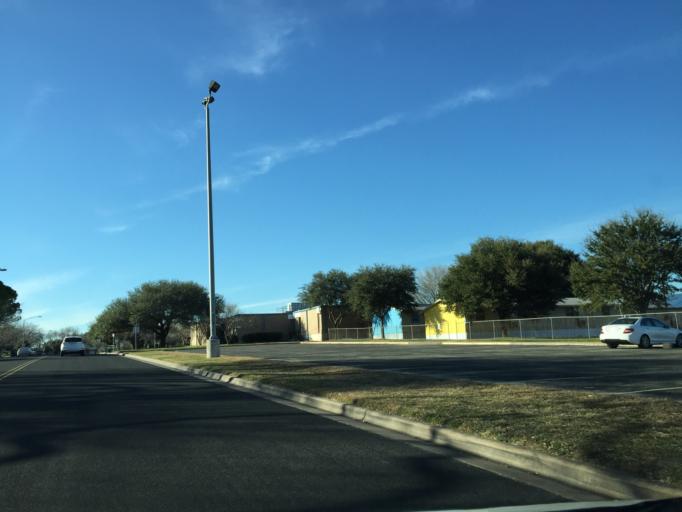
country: US
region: Texas
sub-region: Travis County
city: Onion Creek
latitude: 30.2046
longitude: -97.7884
